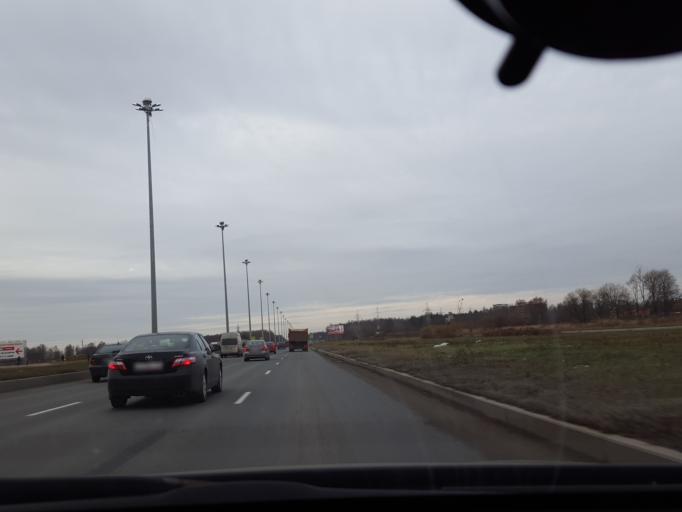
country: RU
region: Leningrad
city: Untolovo
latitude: 60.0395
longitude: 30.2427
